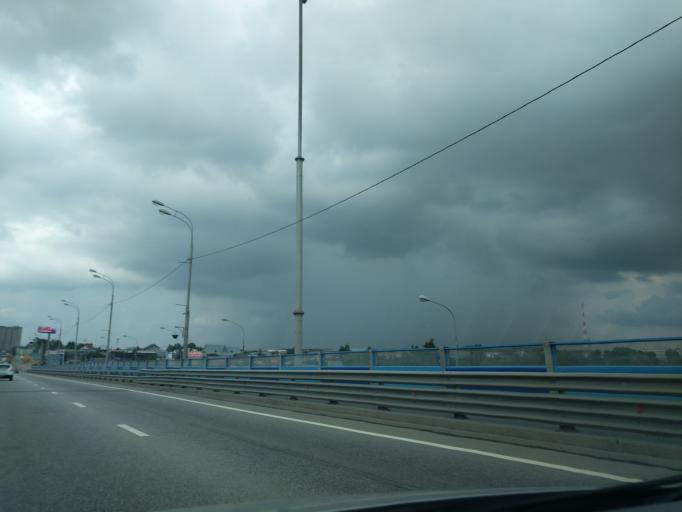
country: RU
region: Moscow
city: Severnyy
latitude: 55.9503
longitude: 37.5390
